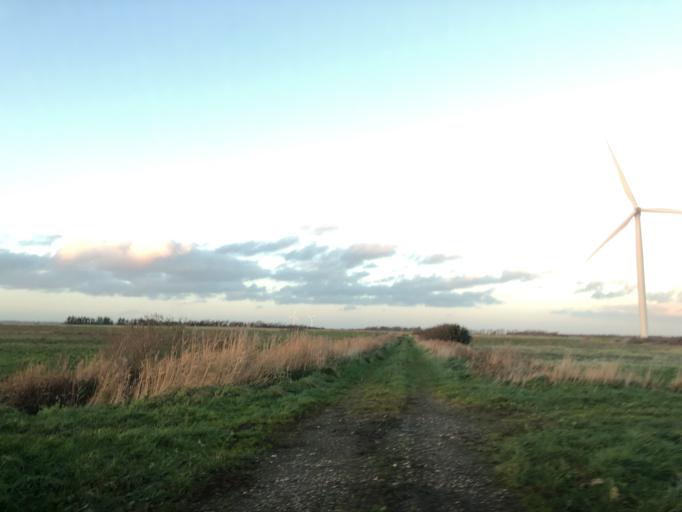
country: DK
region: Central Jutland
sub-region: Holstebro Kommune
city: Ulfborg
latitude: 56.2963
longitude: 8.2961
